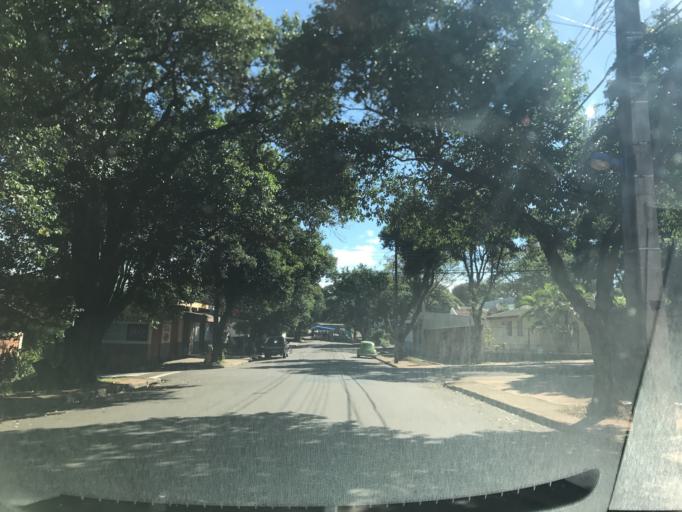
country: BR
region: Parana
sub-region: Maringa
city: Maringa
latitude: -23.4532
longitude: -51.9610
